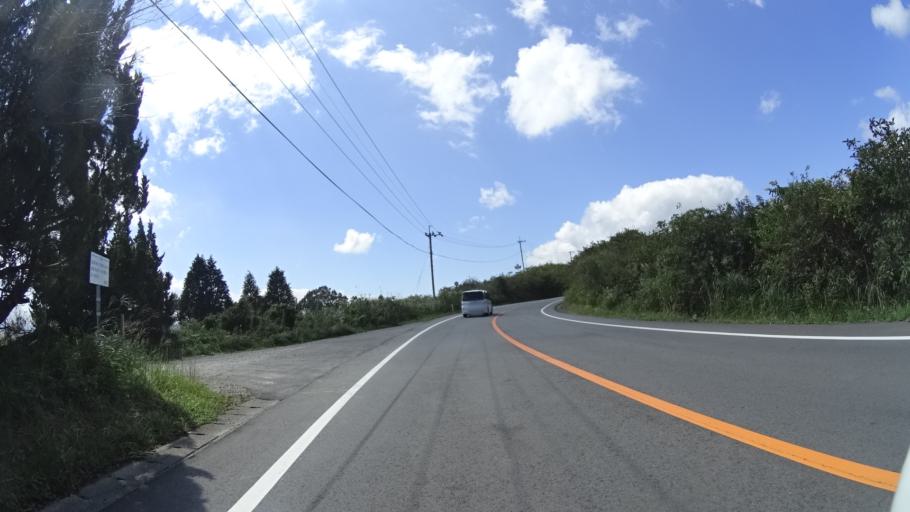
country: JP
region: Kumamoto
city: Aso
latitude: 33.0060
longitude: 131.0979
